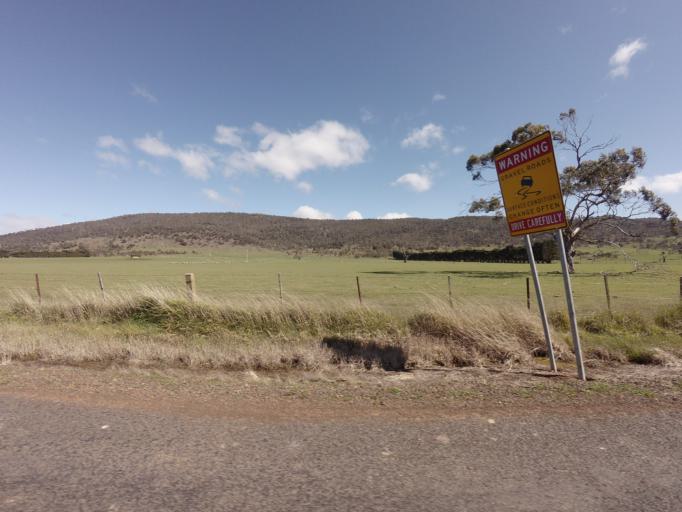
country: AU
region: Tasmania
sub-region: Northern Midlands
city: Evandale
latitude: -41.9629
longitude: 147.4394
